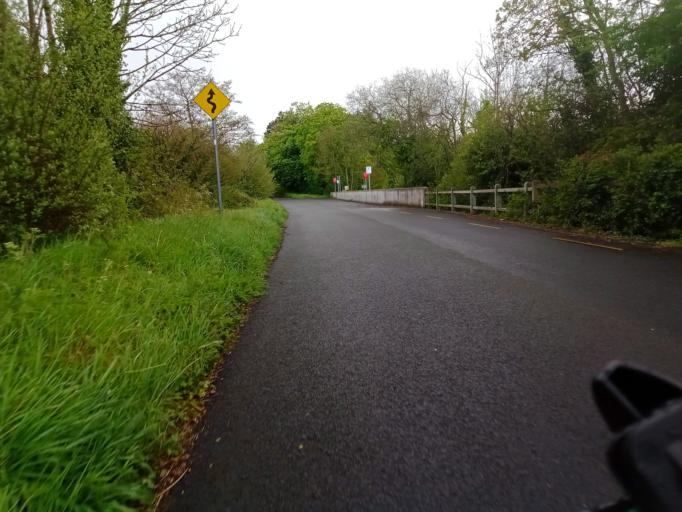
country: IE
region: Leinster
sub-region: Kilkenny
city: Kilkenny
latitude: 52.6756
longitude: -7.2596
